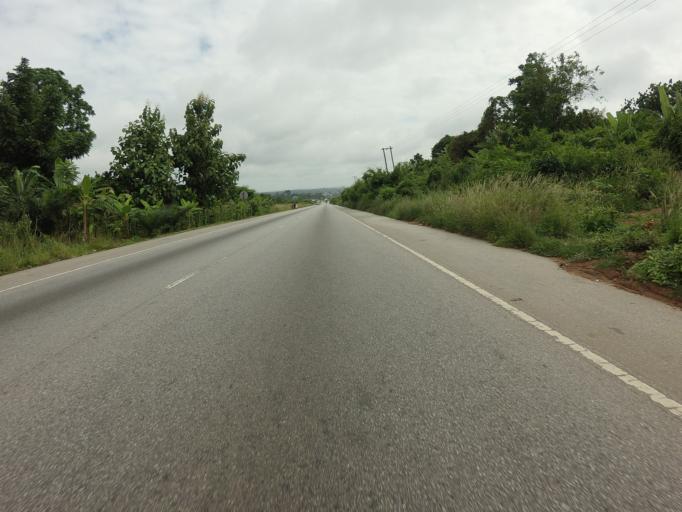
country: GH
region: Ashanti
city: Tafo
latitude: 6.9968
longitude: -1.6972
